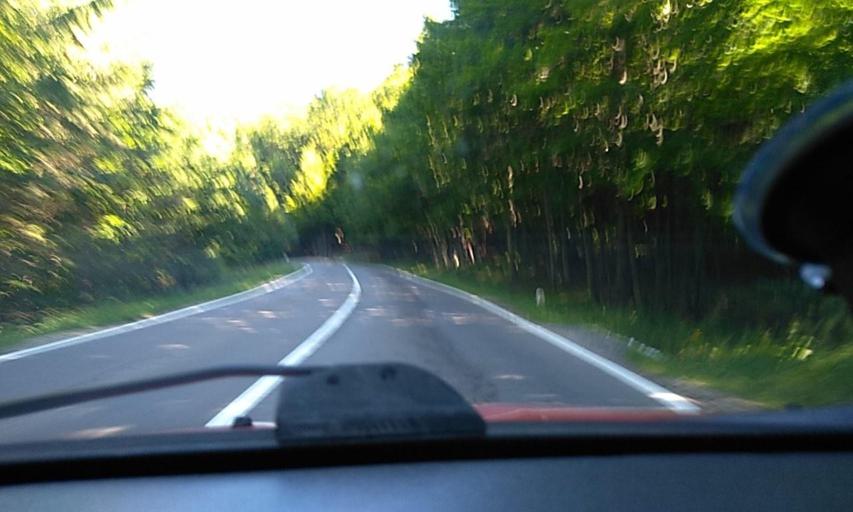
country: RO
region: Brasov
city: Crivina
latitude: 45.4655
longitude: 25.9407
